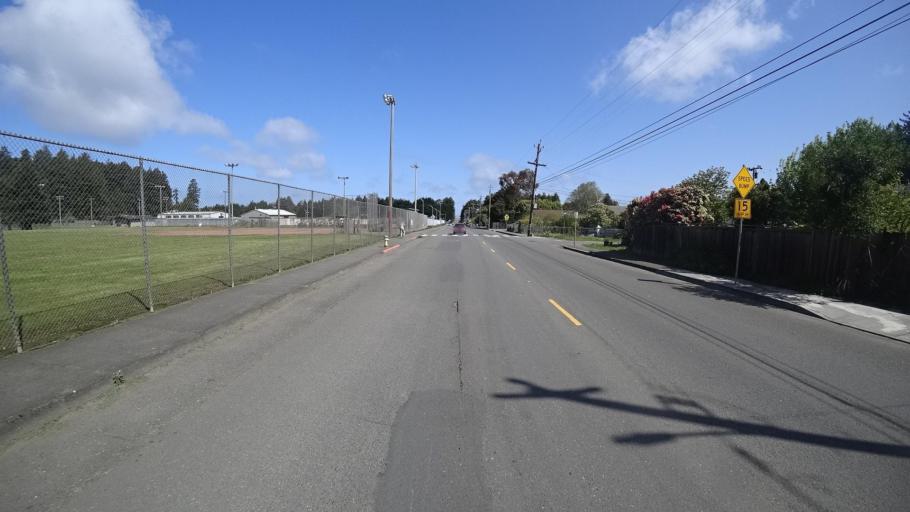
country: US
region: California
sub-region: Humboldt County
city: Cutten
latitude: 40.7747
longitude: -124.1421
